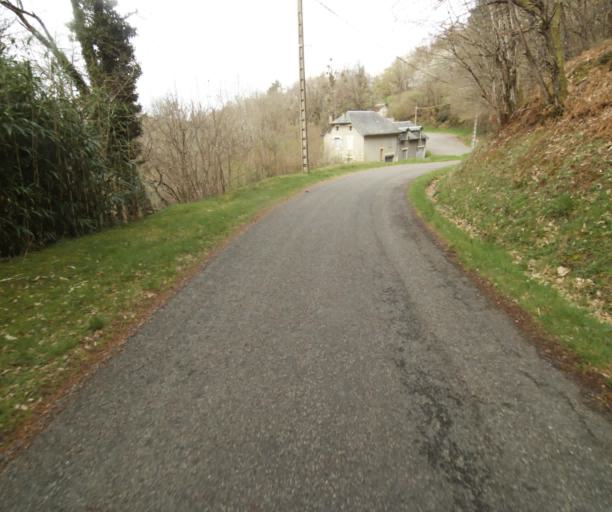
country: FR
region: Limousin
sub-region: Departement de la Correze
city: Laguenne
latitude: 45.2252
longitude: 1.8594
